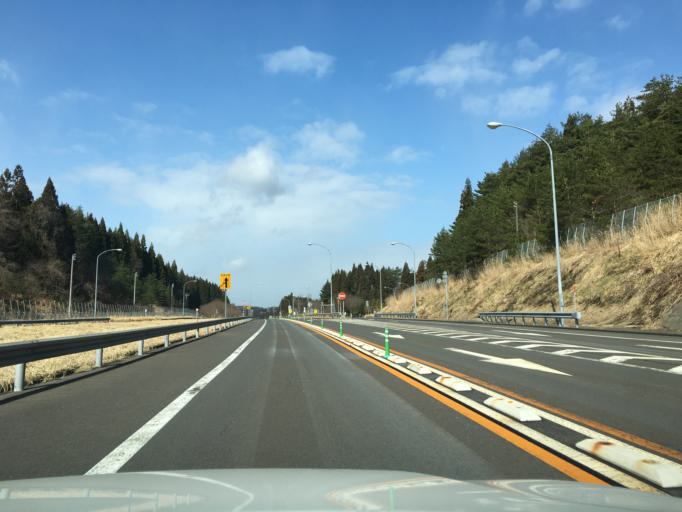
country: JP
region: Akita
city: Akita
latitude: 39.7494
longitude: 140.1523
